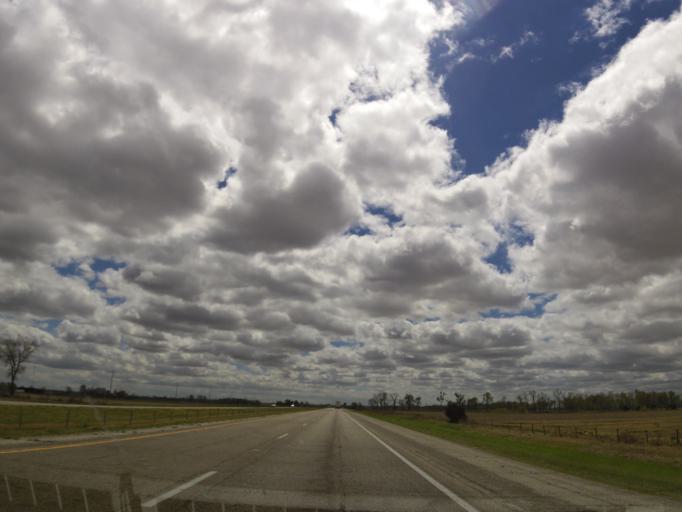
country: US
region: Arkansas
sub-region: Poinsett County
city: Marked Tree
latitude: 35.5814
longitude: -90.4969
